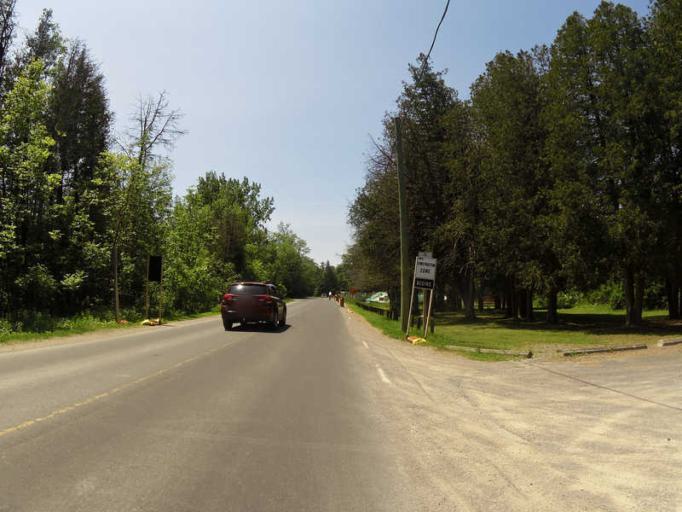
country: CA
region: Ontario
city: Peterborough
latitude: 44.3896
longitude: -78.2683
